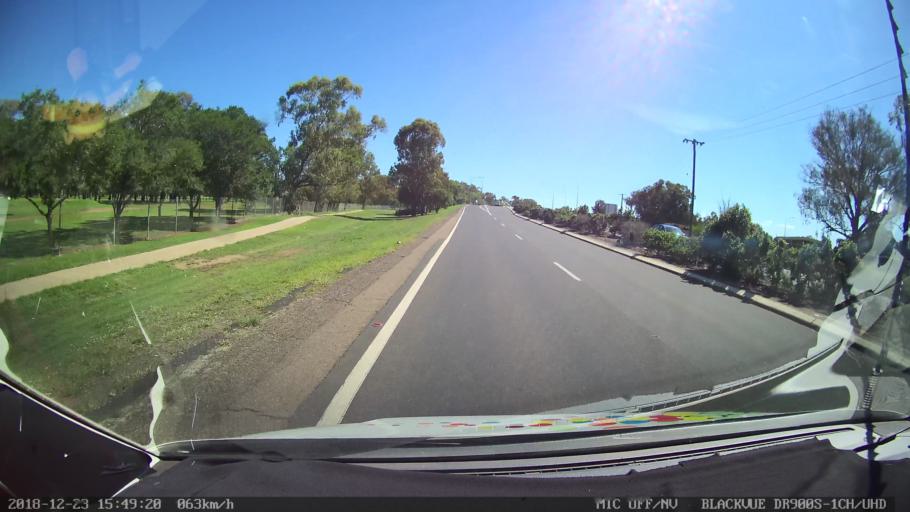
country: AU
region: New South Wales
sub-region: Tamworth Municipality
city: South Tamworth
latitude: -31.0985
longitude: 150.9073
